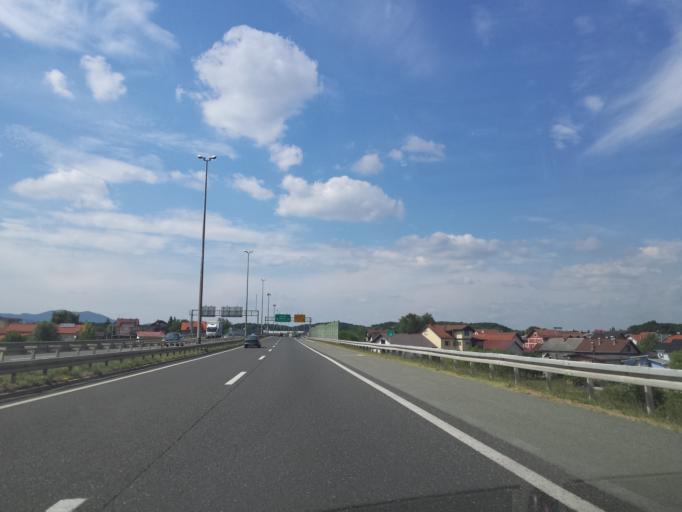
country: HR
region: Grad Zagreb
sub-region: Sesvete
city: Sesvete
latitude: 45.8223
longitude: 16.1380
